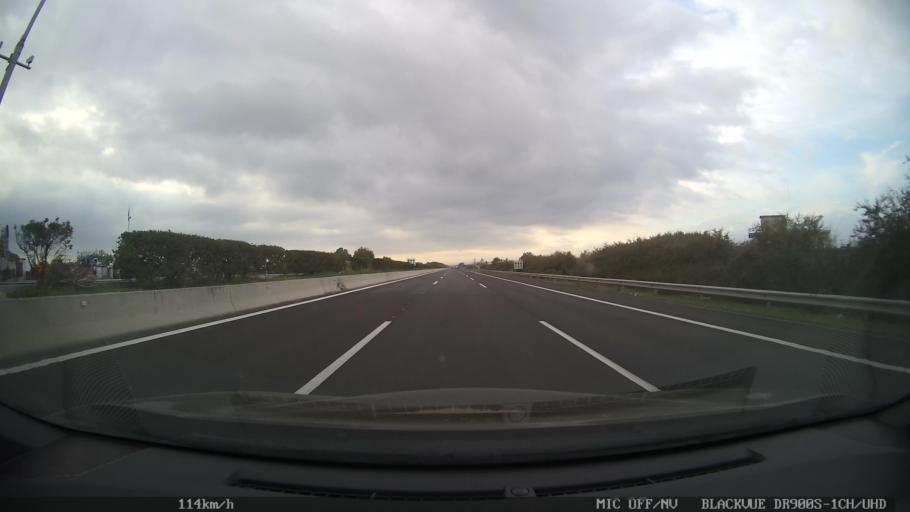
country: GR
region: Central Macedonia
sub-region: Nomos Pierias
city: Peristasi
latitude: 40.2427
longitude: 22.5353
